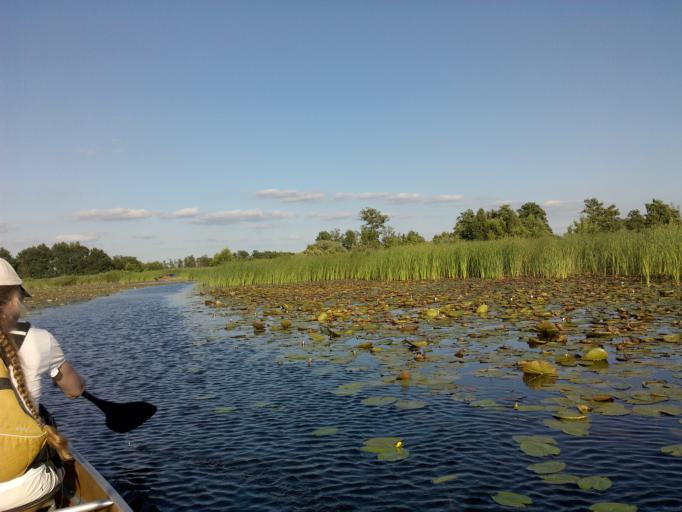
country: NL
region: Overijssel
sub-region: Gemeente Steenwijkerland
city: Sint Jansklooster
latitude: 52.6625
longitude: 6.0626
